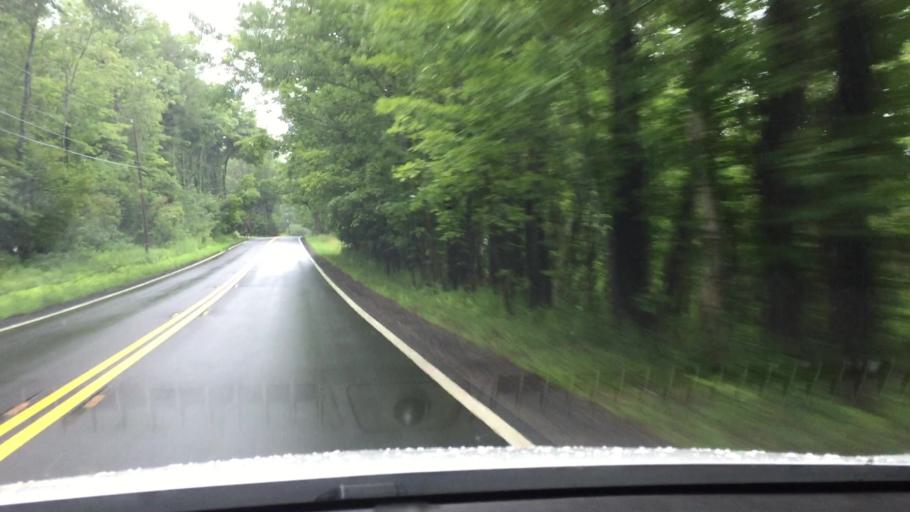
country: US
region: Massachusetts
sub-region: Berkshire County
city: Becket
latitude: 42.3408
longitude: -73.1128
